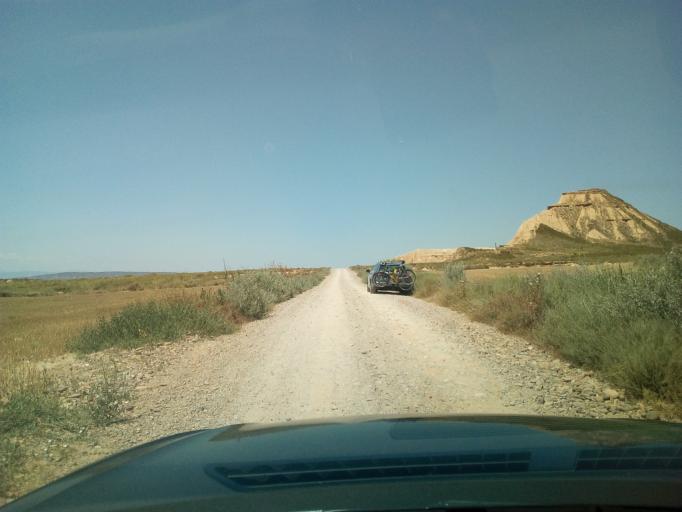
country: ES
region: Aragon
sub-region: Provincia de Zaragoza
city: Sadaba
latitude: 42.1948
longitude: -1.4162
